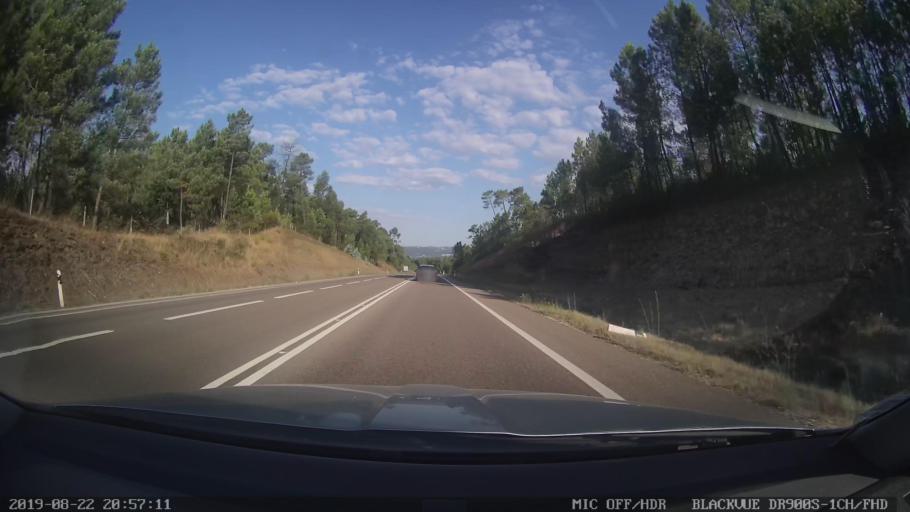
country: PT
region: Castelo Branco
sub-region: Serta
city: Serta
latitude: 39.7923
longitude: -8.0616
